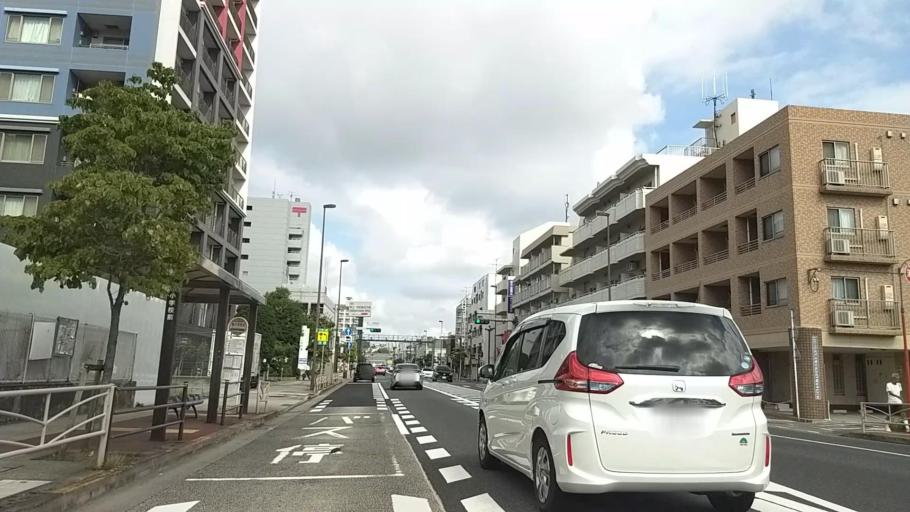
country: JP
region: Kanagawa
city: Yokohama
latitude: 35.4603
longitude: 139.5980
